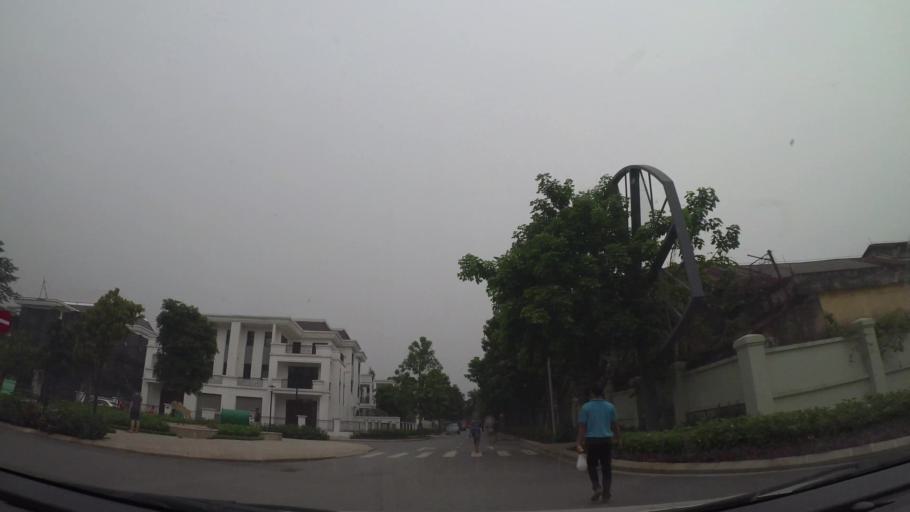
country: VN
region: Ha Noi
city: Cau Dien
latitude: 21.0383
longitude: 105.7618
